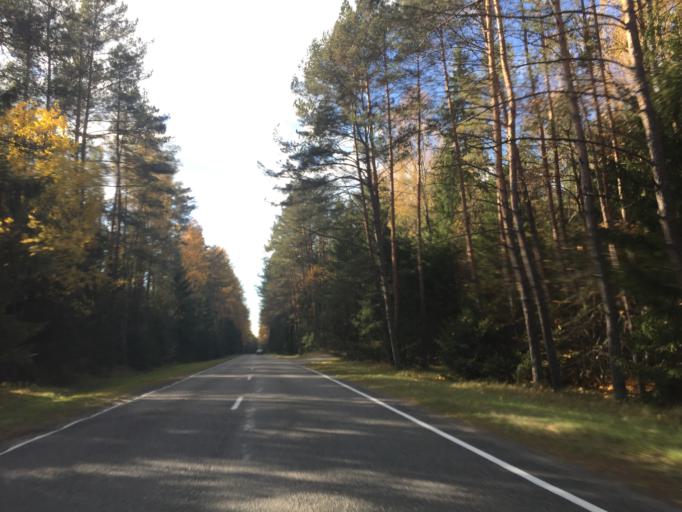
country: BY
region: Minsk
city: Narach
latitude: 54.9458
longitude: 26.5800
